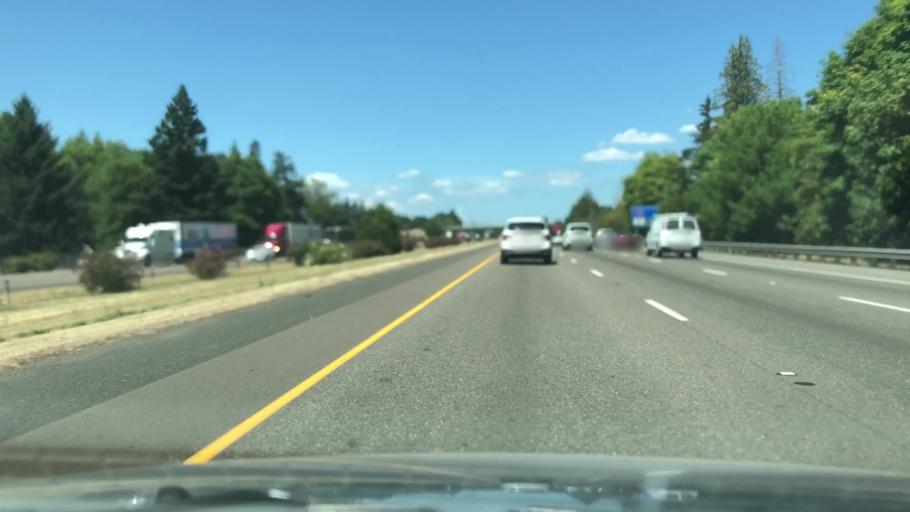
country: US
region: Oregon
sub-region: Clackamas County
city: Wilsonville
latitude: 45.3124
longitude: -122.7690
